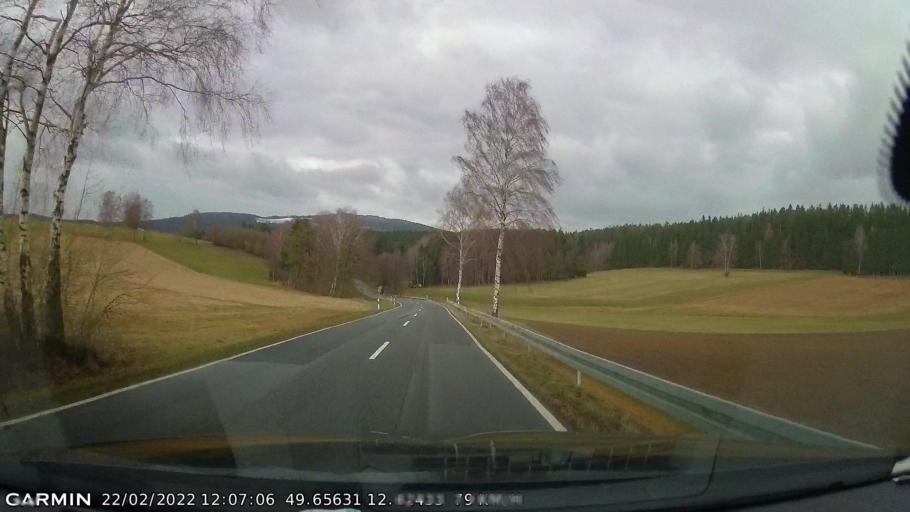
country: DE
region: Bavaria
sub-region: Upper Palatinate
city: Pleystein
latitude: 49.6564
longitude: 12.4241
